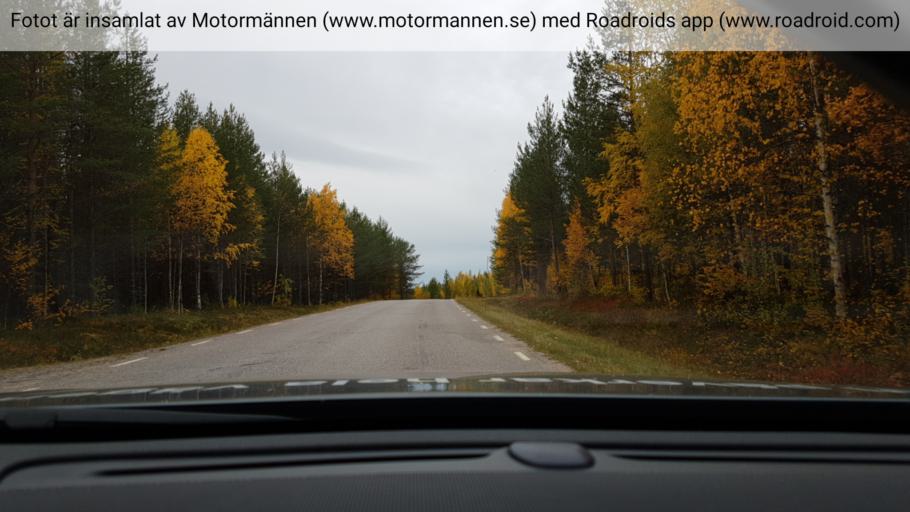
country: SE
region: Norrbotten
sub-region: Overkalix Kommun
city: OEverkalix
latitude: 66.2314
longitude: 22.9941
